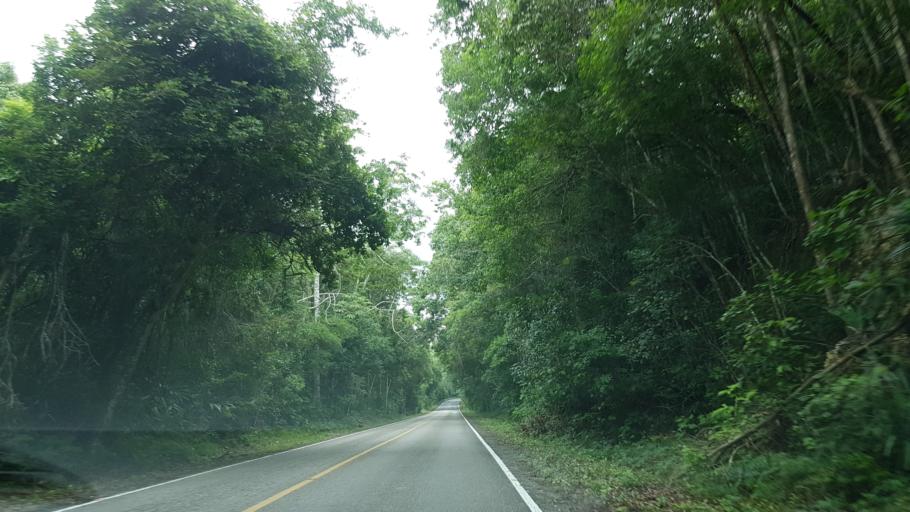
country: GT
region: Peten
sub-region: Municipio de San Jose
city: San Jose
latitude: 17.1723
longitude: -89.6428
